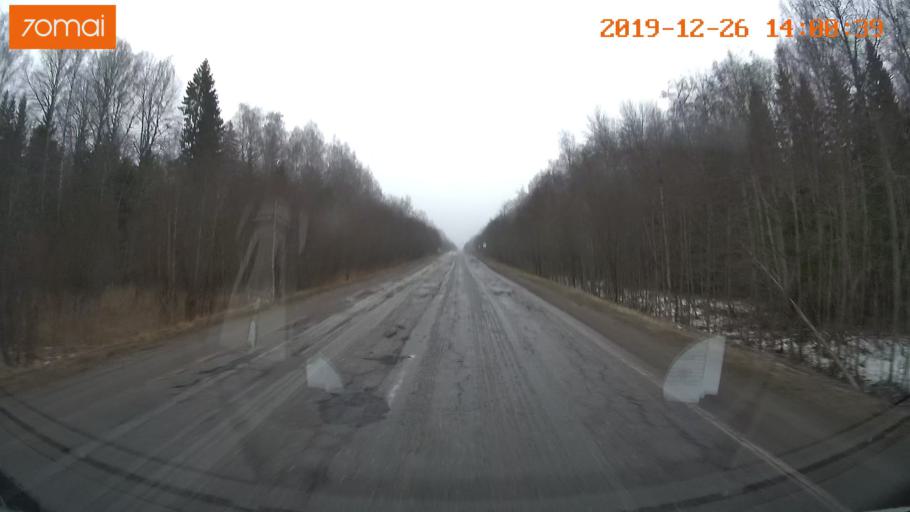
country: RU
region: Jaroslavl
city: Poshekhon'ye
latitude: 58.5565
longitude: 38.7477
